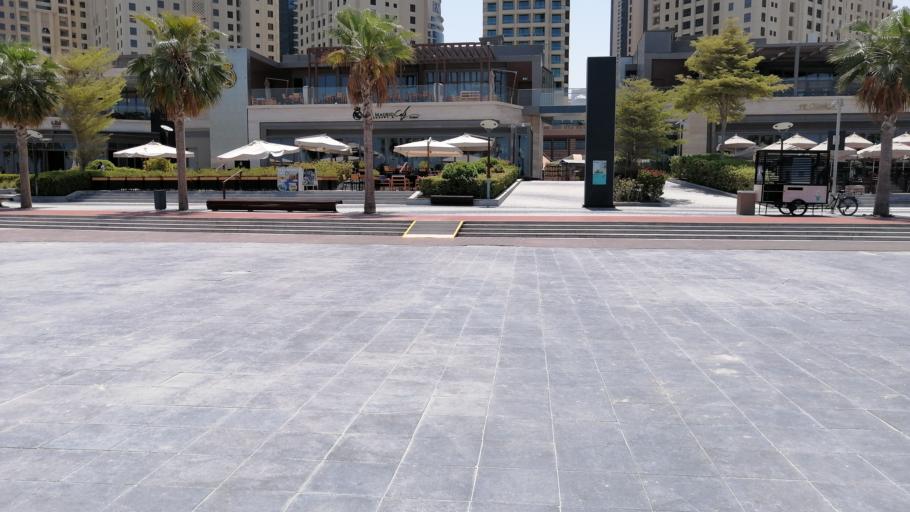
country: AE
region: Dubai
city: Dubai
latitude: 25.0765
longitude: 55.1305
